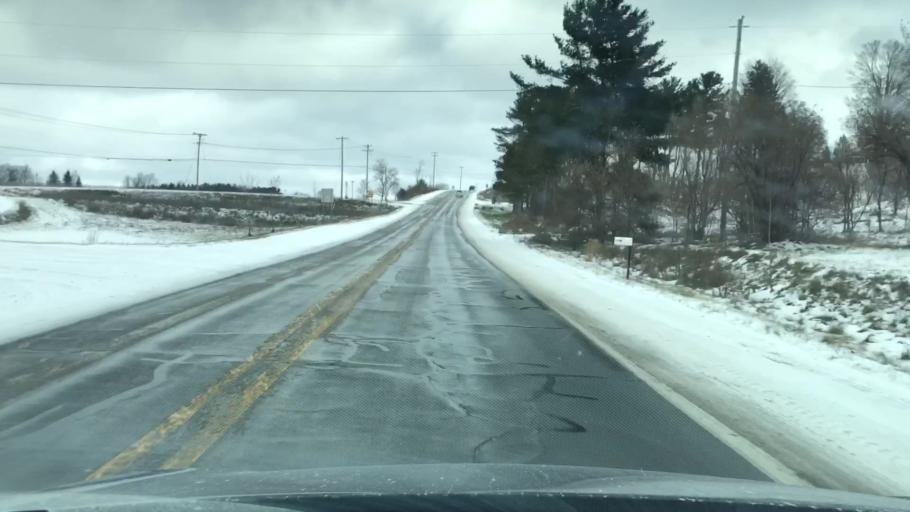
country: US
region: Michigan
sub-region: Antrim County
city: Elk Rapids
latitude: 44.8604
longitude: -85.5219
